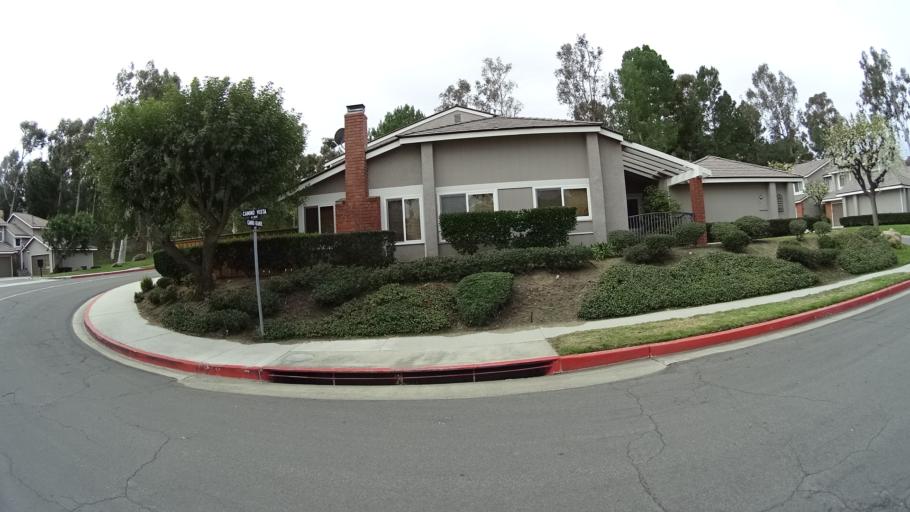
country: US
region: California
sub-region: Orange County
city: Villa Park
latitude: 33.8393
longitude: -117.7592
